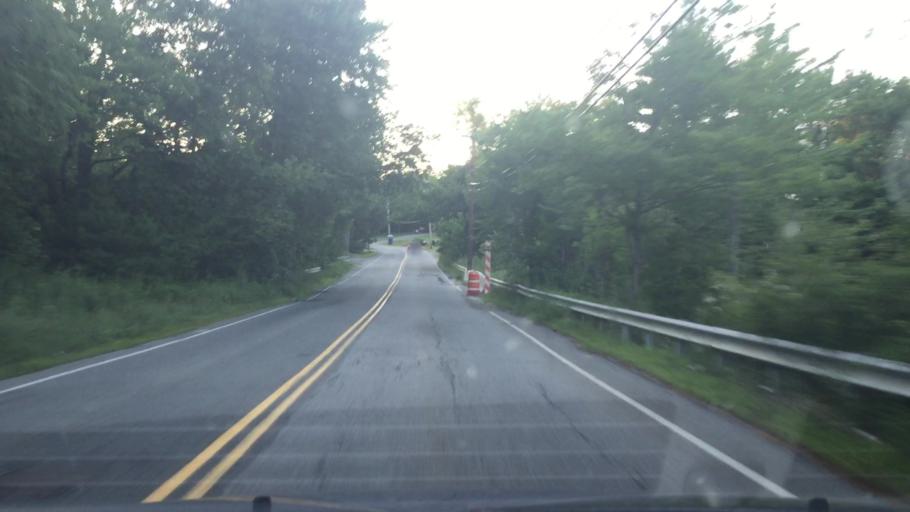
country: US
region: Massachusetts
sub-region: Essex County
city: Haverhill
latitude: 42.8063
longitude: -71.0854
